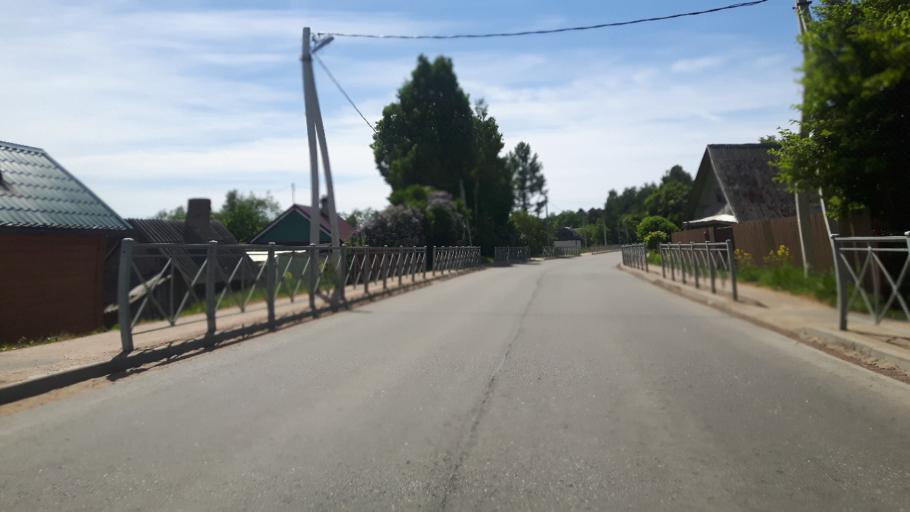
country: RU
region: Leningrad
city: Ust'-Luga
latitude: 59.5846
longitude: 28.1900
